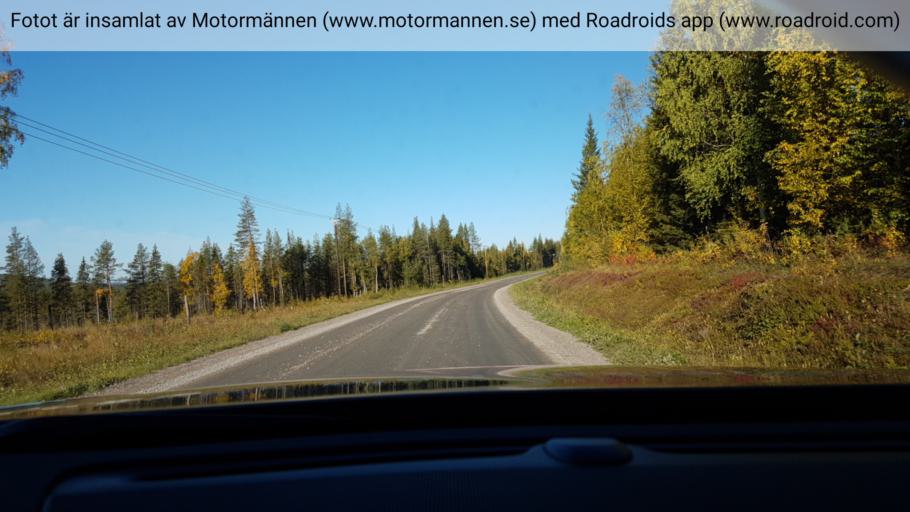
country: SE
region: Norrbotten
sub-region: Alvsbyns Kommun
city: AElvsbyn
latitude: 66.1815
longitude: 21.2228
